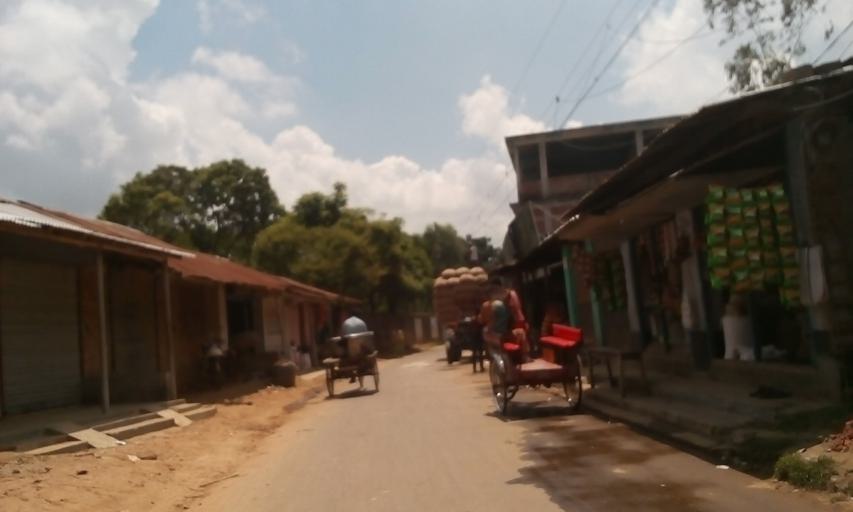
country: IN
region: West Bengal
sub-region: Dakshin Dinajpur
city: Balurghat
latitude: 25.3782
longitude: 88.9920
